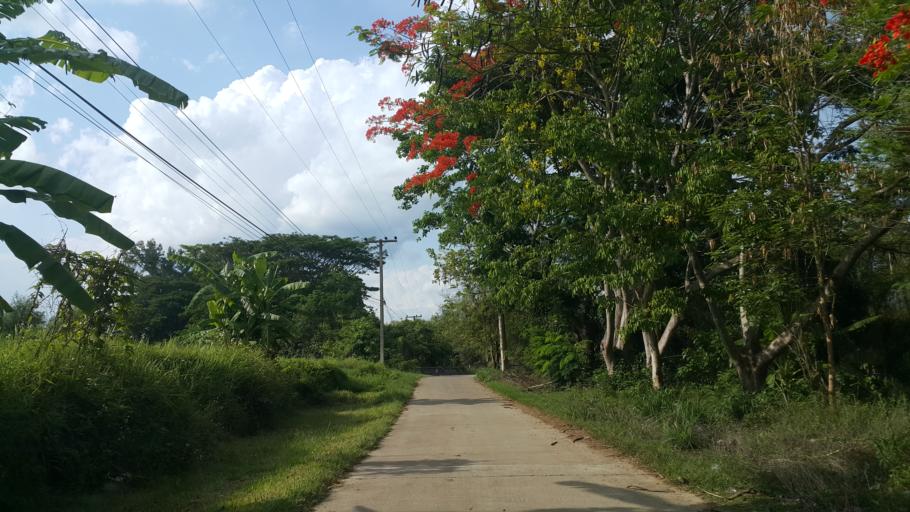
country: TH
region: Chiang Mai
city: Mae On
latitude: 18.7919
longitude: 99.2593
